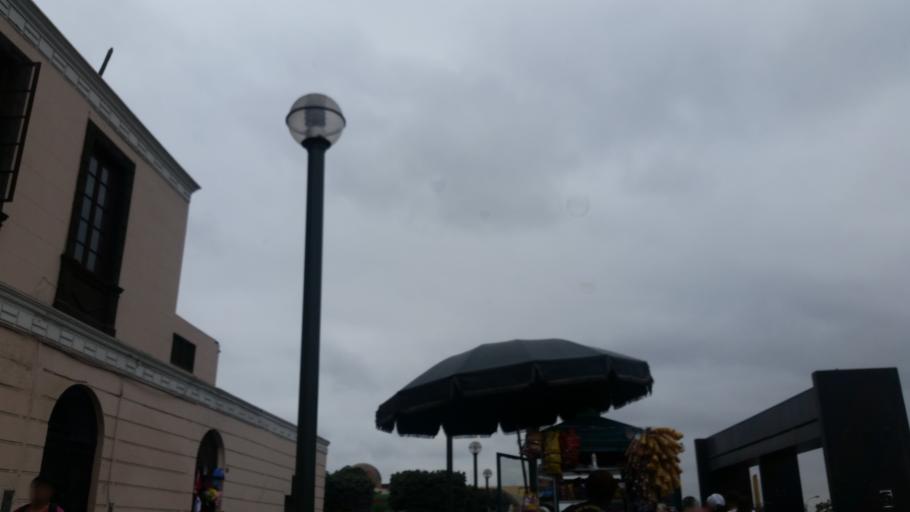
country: PE
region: Lima
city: Lima
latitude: -12.0438
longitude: -77.0306
